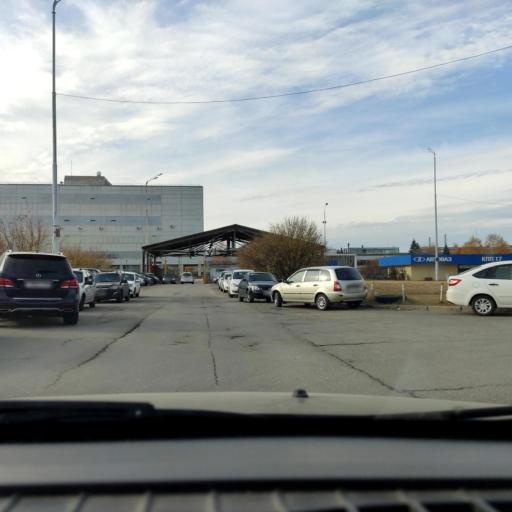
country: RU
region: Samara
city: Tol'yatti
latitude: 53.5575
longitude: 49.2867
